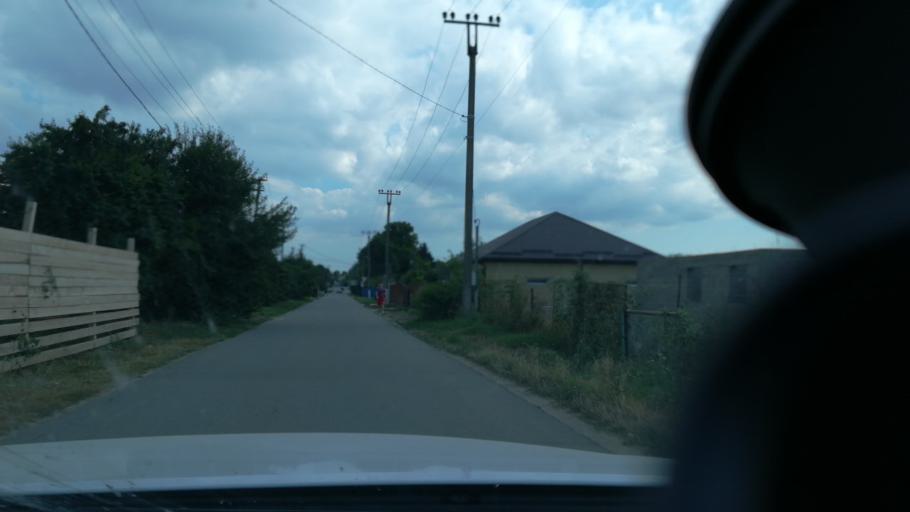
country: RU
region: Krasnodarskiy
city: Yurovka
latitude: 45.1183
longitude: 37.4152
